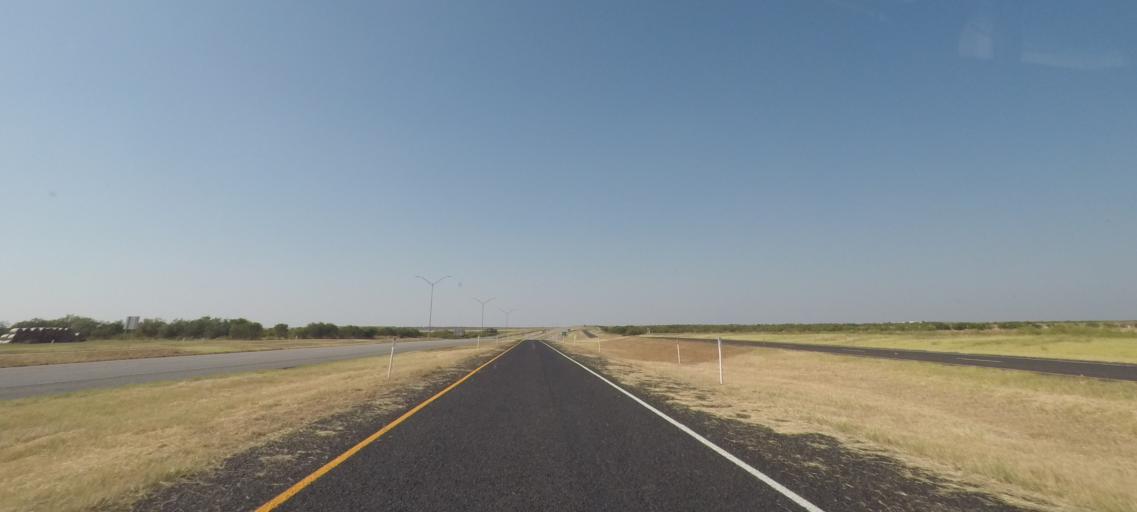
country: US
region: Texas
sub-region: Baylor County
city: Seymour
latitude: 33.6001
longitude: -99.2414
